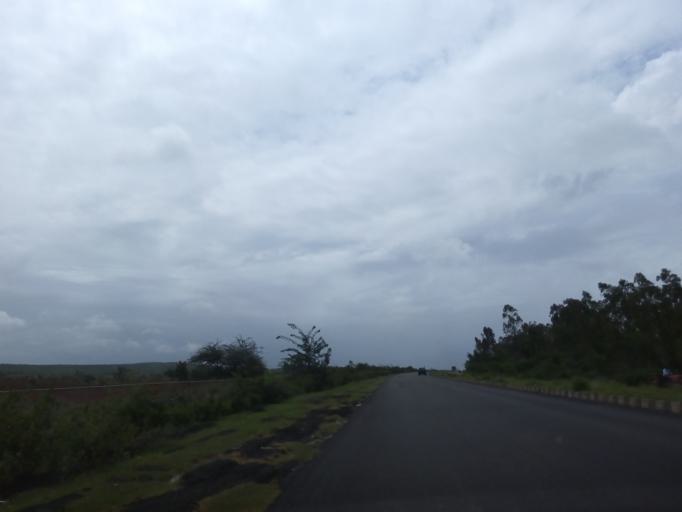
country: IN
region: Karnataka
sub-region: Haveri
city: Byadgi
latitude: 14.7102
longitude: 75.5091
